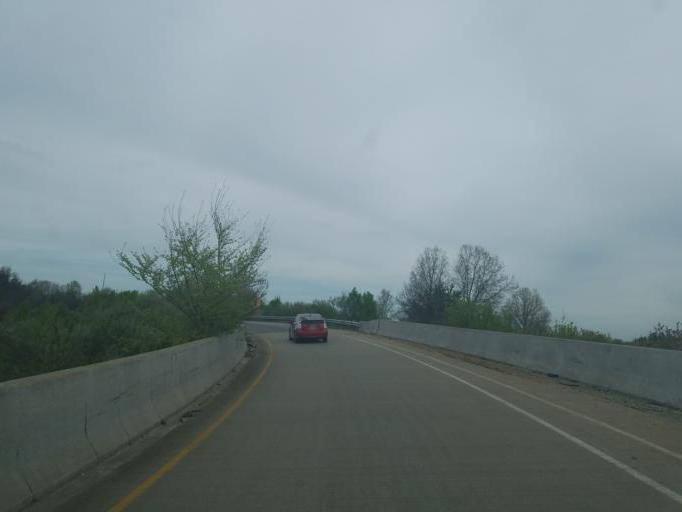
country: US
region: Ohio
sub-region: Summit County
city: Norton
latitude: 40.9944
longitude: -81.6605
